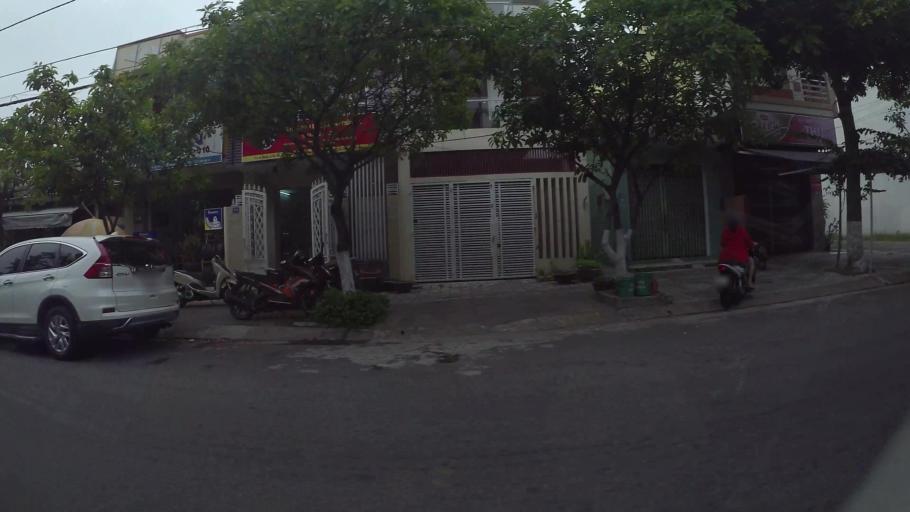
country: VN
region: Da Nang
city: Cam Le
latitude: 16.0343
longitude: 108.2144
